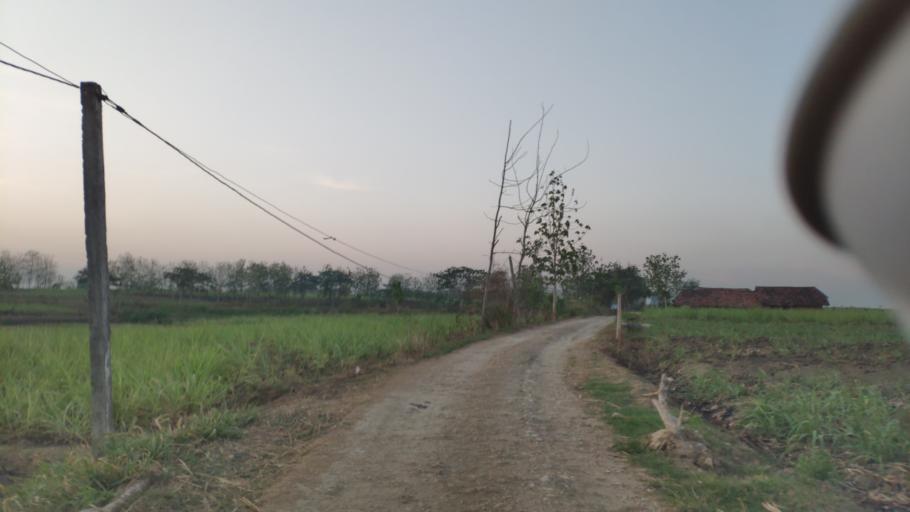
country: ID
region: Central Java
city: Jepang
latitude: -7.0326
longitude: 111.2388
